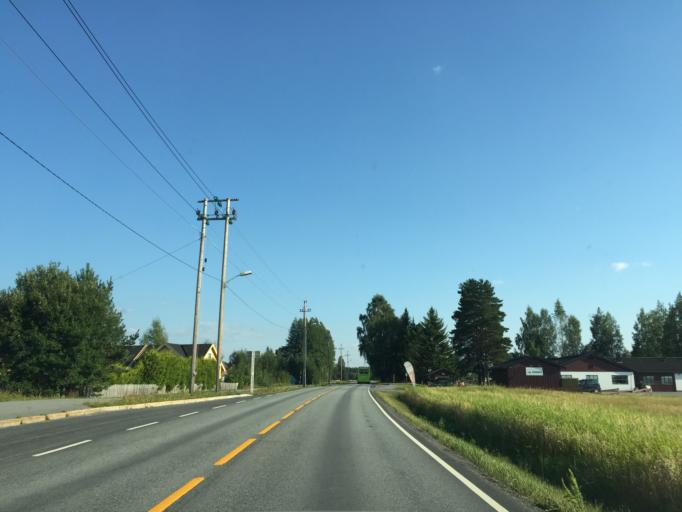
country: NO
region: Akershus
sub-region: Nes
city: Arnes
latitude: 60.1087
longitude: 11.4769
